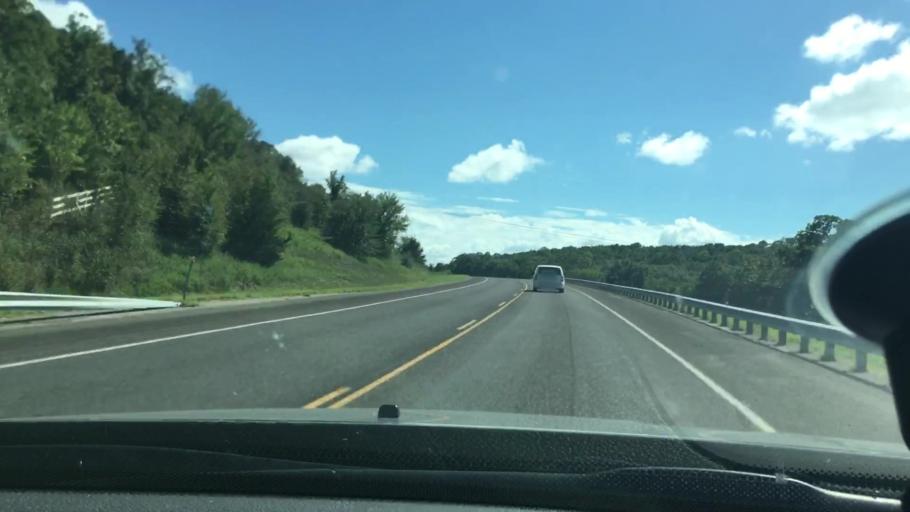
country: US
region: Oklahoma
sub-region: Sequoyah County
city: Vian
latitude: 35.5290
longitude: -94.9739
